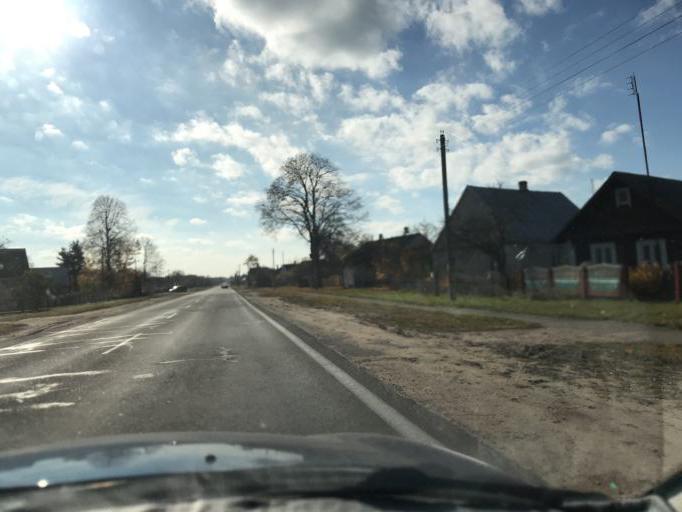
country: LT
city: Salcininkai
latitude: 54.2572
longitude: 25.3570
